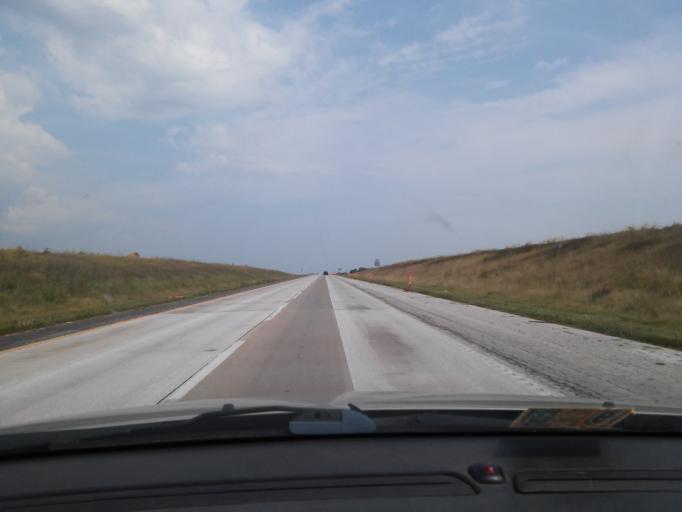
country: US
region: Missouri
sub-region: Audrain County
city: Mexico
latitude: 39.0660
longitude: -91.8956
